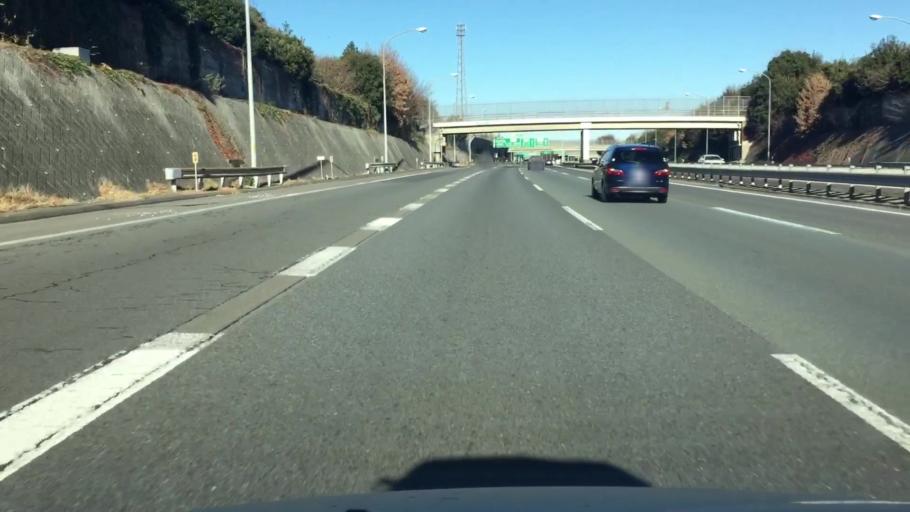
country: JP
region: Saitama
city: Sakado
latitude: 35.9260
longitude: 139.4107
